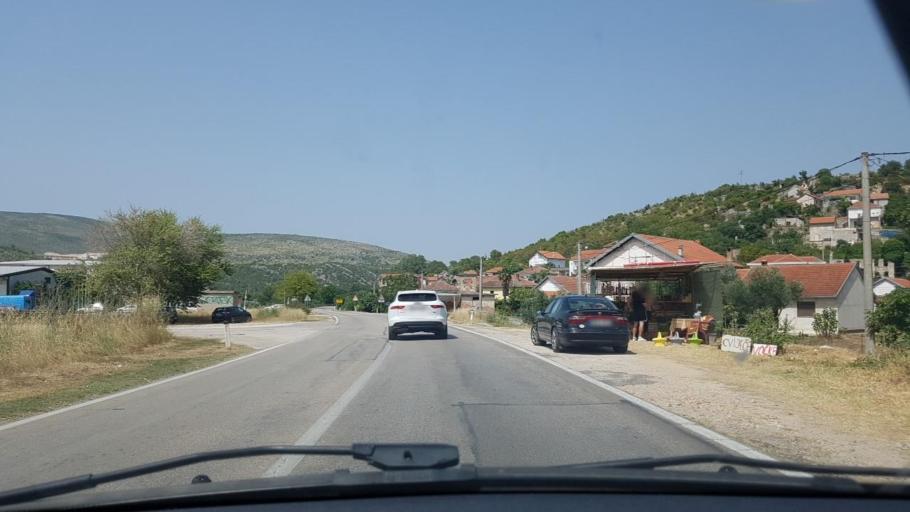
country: BA
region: Federation of Bosnia and Herzegovina
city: Tasovcici
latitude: 43.1172
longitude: 17.7137
